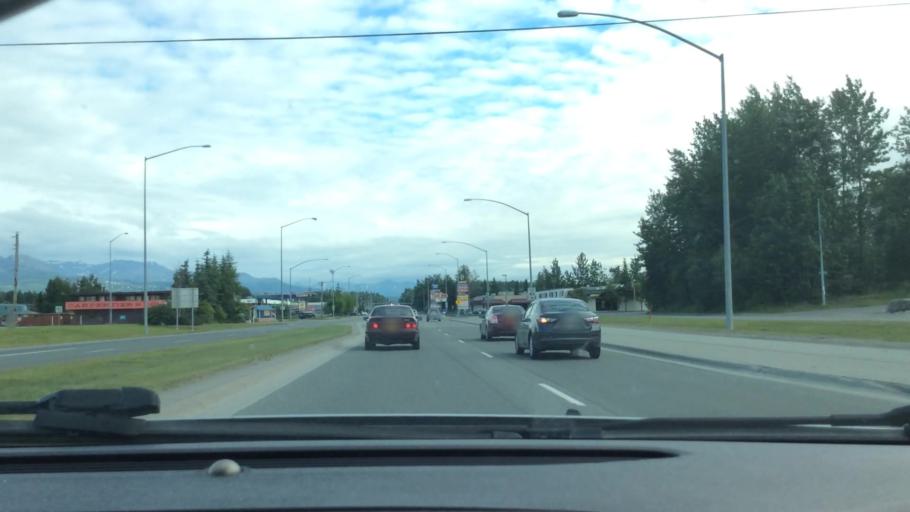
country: US
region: Alaska
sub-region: Anchorage Municipality
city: Anchorage
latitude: 61.2239
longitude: -149.7785
